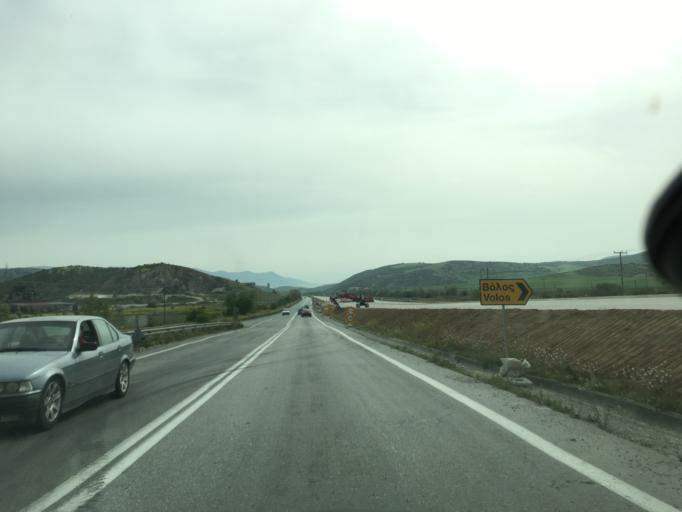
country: GR
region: Thessaly
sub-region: Nomos Magnisias
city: Velestino
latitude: 39.3862
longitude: 22.7915
